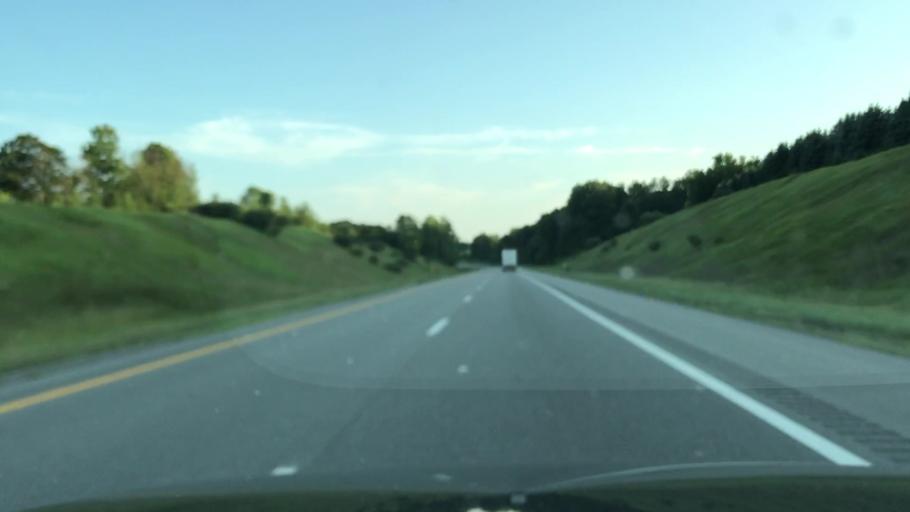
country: US
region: Michigan
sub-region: Osceola County
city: Reed City
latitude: 43.8696
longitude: -85.5329
